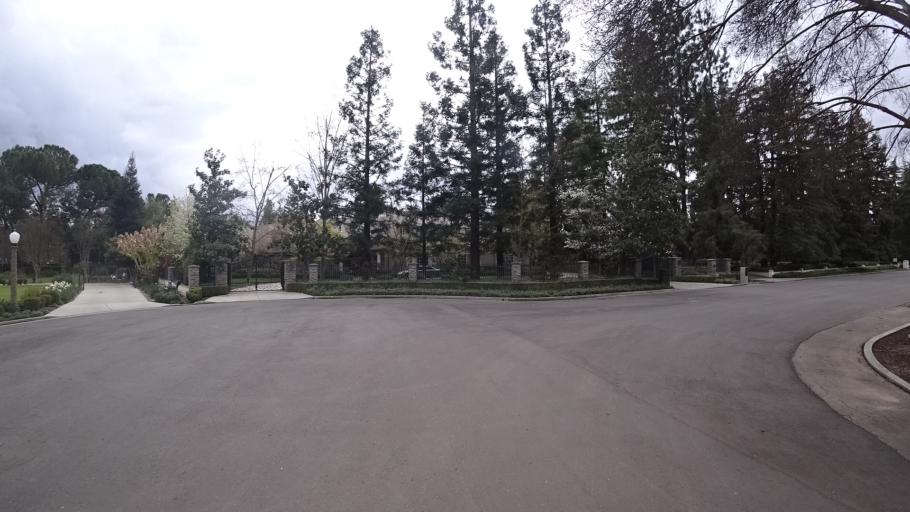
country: US
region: California
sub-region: Fresno County
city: Fresno
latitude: 36.8453
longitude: -119.8318
